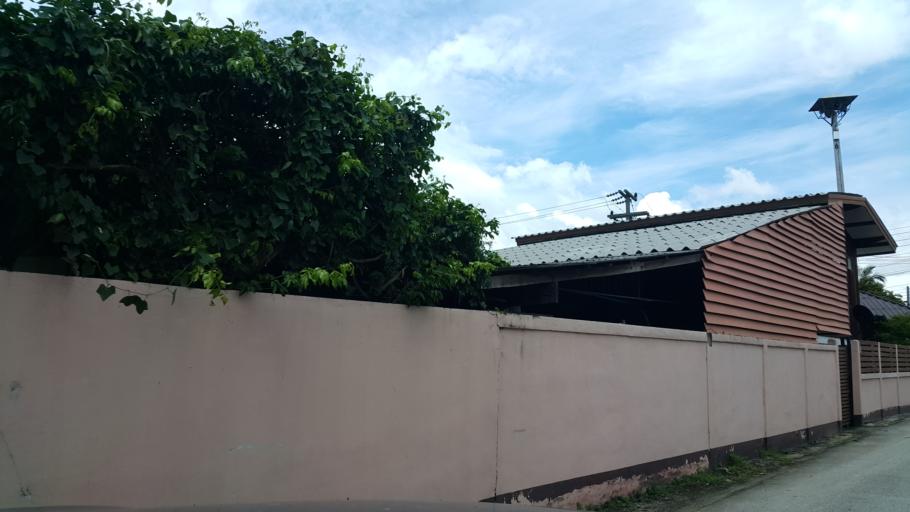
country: TH
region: Chiang Mai
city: San Kamphaeng
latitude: 18.7437
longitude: 99.1333
